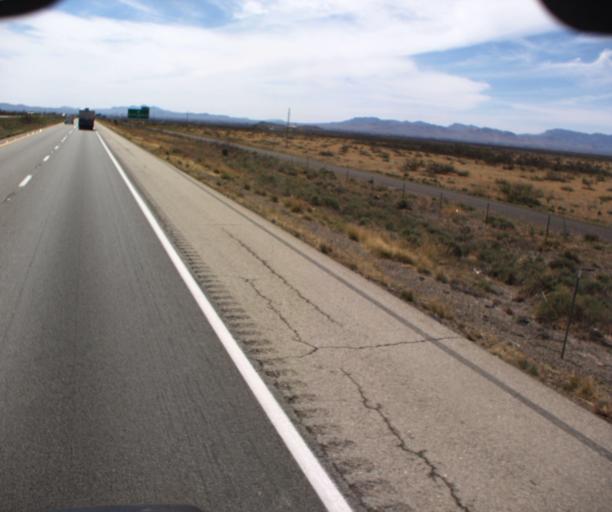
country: US
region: Arizona
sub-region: Cochise County
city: Willcox
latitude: 32.3243
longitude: -109.7762
